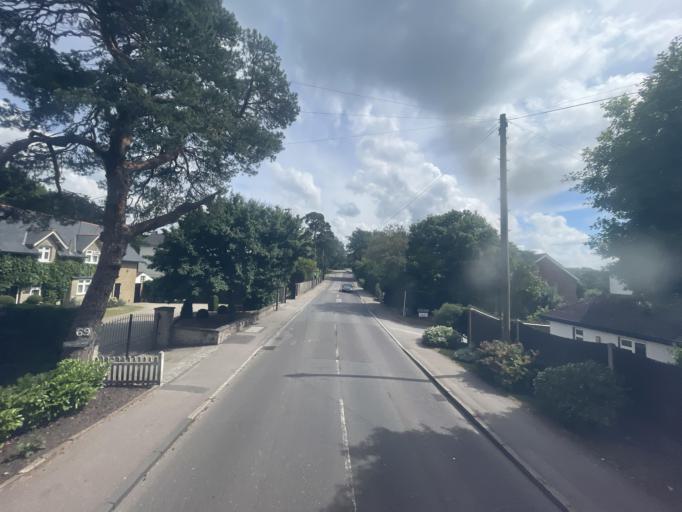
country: GB
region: England
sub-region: Kent
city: Biggin Hill
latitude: 51.3595
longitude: 0.0306
